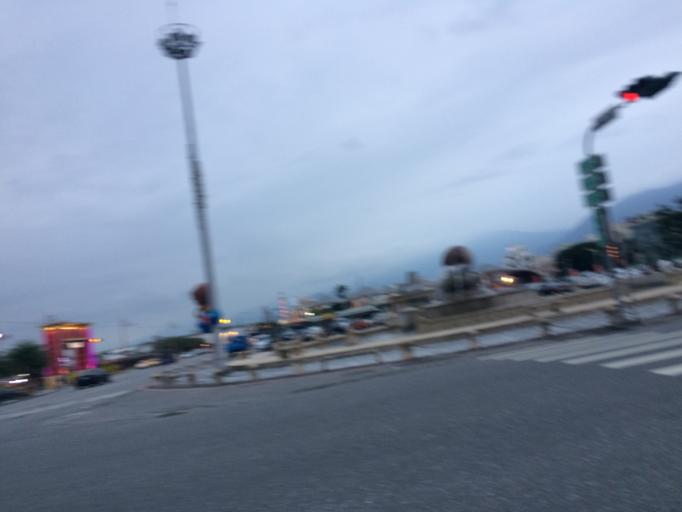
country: TW
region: Taiwan
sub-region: Hualien
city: Hualian
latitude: 23.9743
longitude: 121.6116
